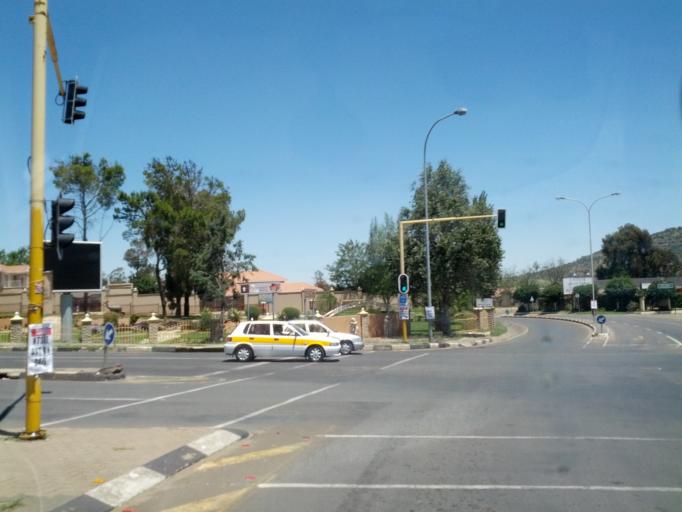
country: LS
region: Maseru
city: Maseru
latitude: -29.3043
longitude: 27.4671
